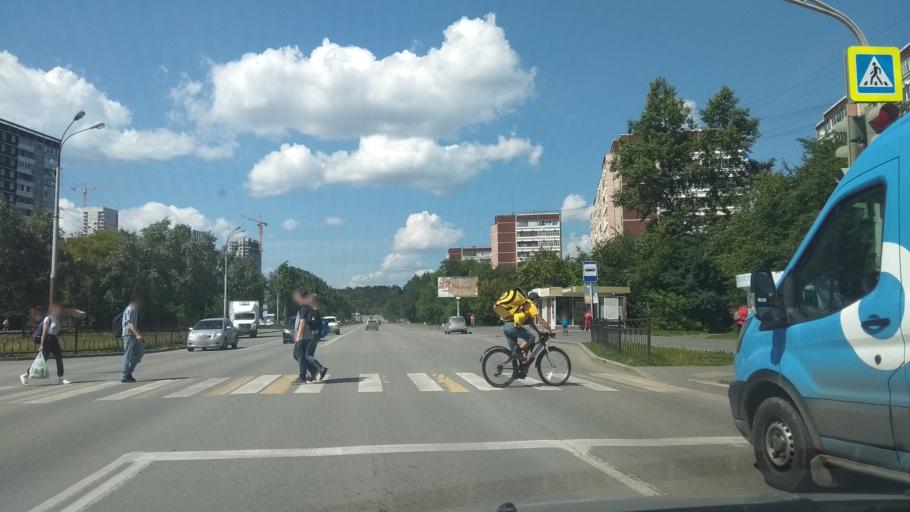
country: RU
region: Sverdlovsk
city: Yekaterinburg
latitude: 56.8370
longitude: 60.6806
